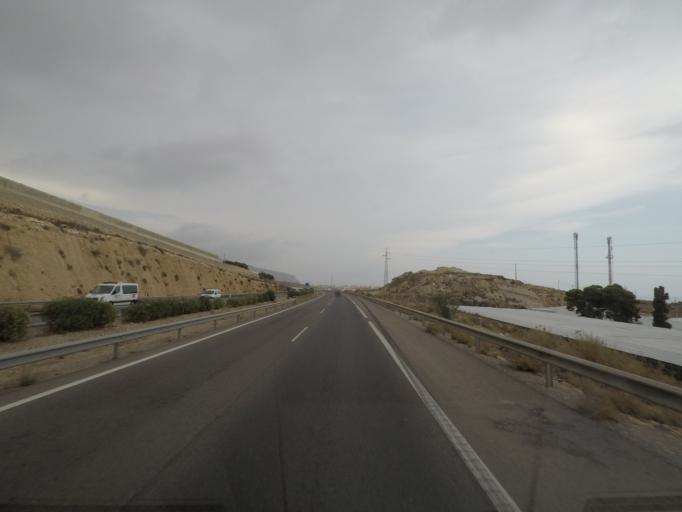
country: ES
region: Andalusia
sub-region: Provincia de Almeria
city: Vicar
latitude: 36.8124
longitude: -2.6174
